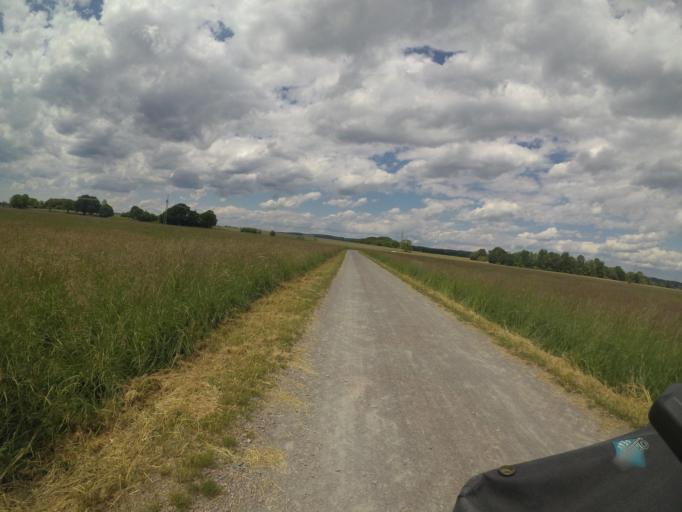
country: DE
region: Rheinland-Pfalz
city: Hauptstuhl
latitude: 49.4021
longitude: 7.4607
